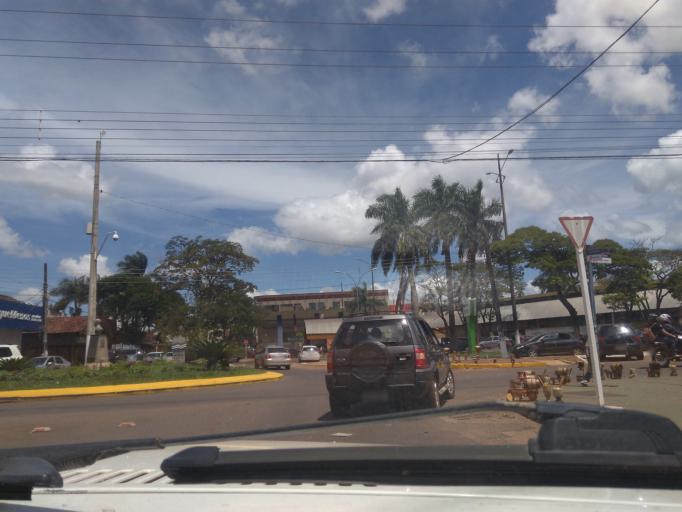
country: BR
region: Mato Grosso do Sul
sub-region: Ponta Pora
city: Ponta Pora
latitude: -22.5383
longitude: -55.7299
